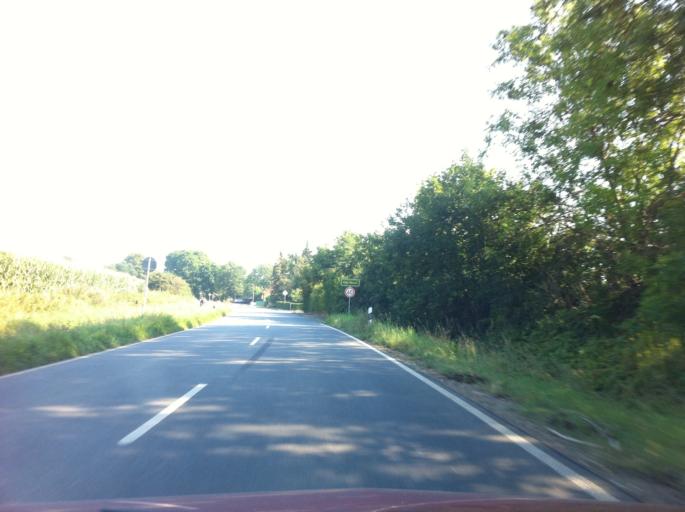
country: DE
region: Schleswig-Holstein
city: Harmsdorf
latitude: 54.3066
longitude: 10.8284
